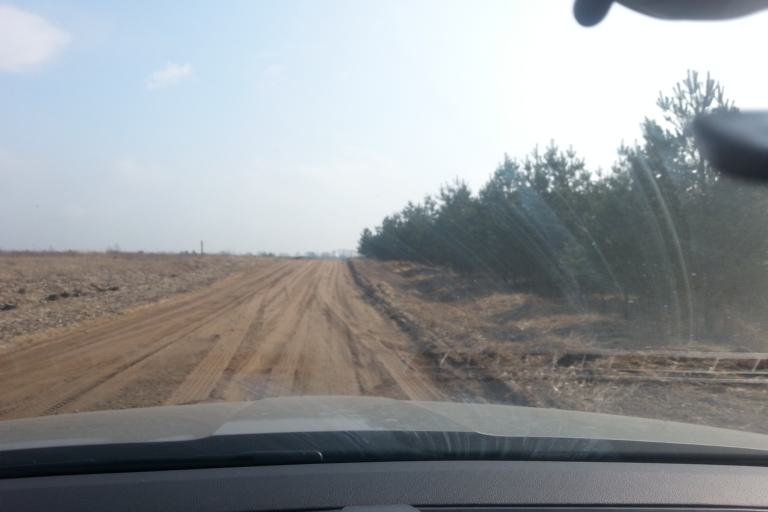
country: LT
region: Vilnius County
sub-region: Trakai
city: Rudiskes
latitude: 54.5005
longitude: 24.9655
